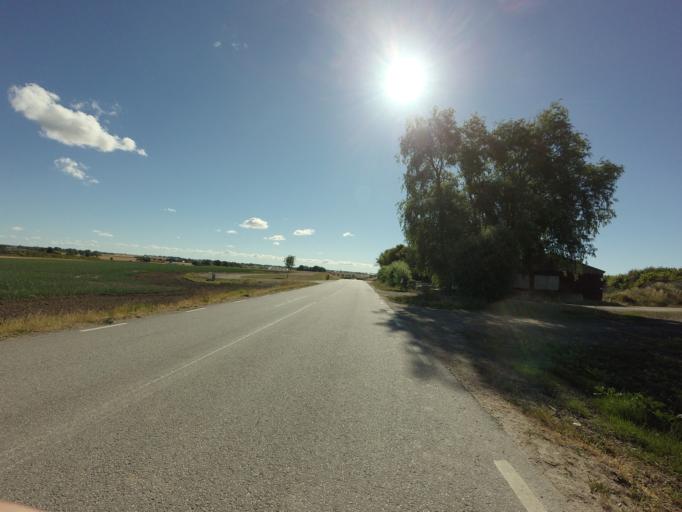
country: SE
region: Skane
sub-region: Trelleborgs Kommun
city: Skare
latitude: 55.3901
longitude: 13.0702
